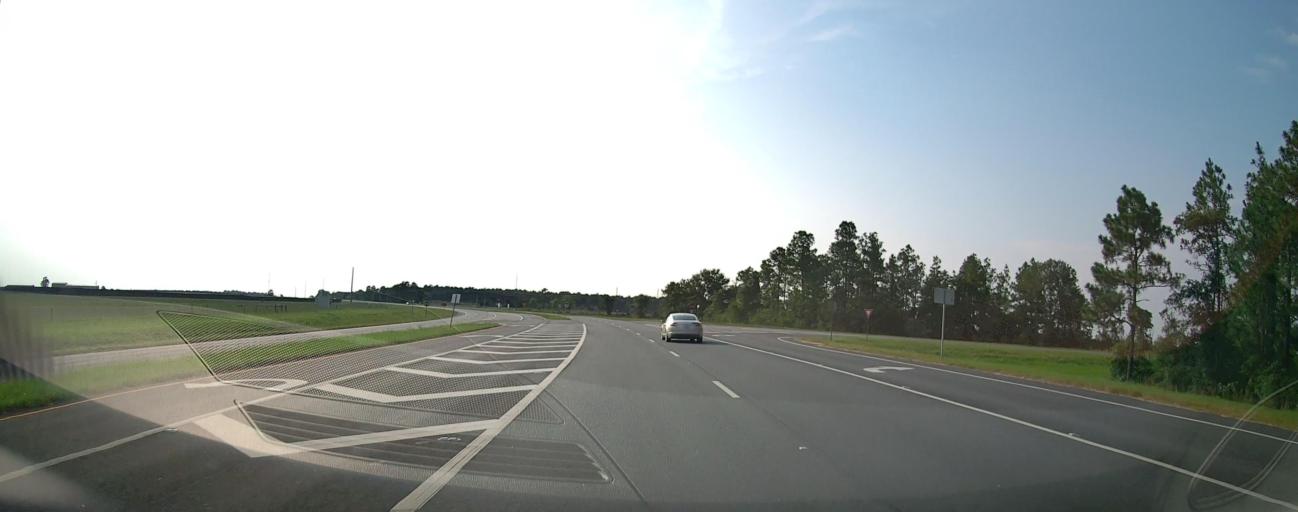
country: US
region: Georgia
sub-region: Taylor County
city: Butler
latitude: 32.5658
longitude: -84.2700
